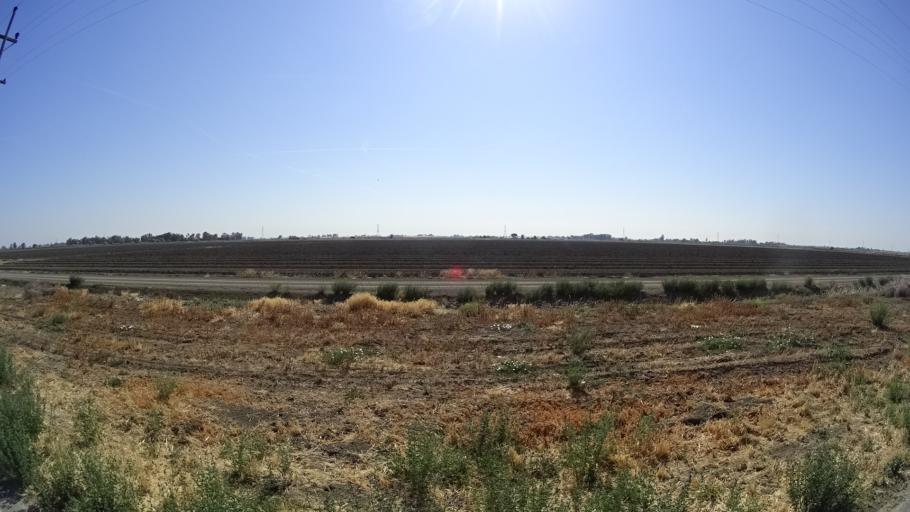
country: US
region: California
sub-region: Kings County
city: Lemoore Station
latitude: 36.3456
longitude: -119.9054
